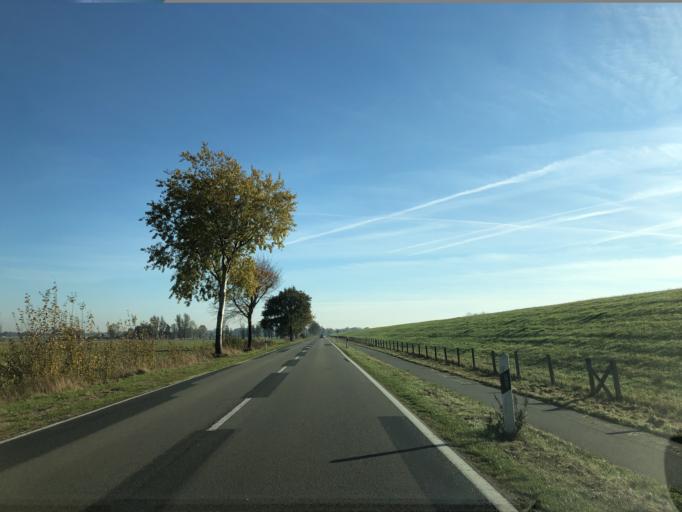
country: DE
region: Lower Saxony
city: Rhede
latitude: 53.0595
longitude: 7.2977
